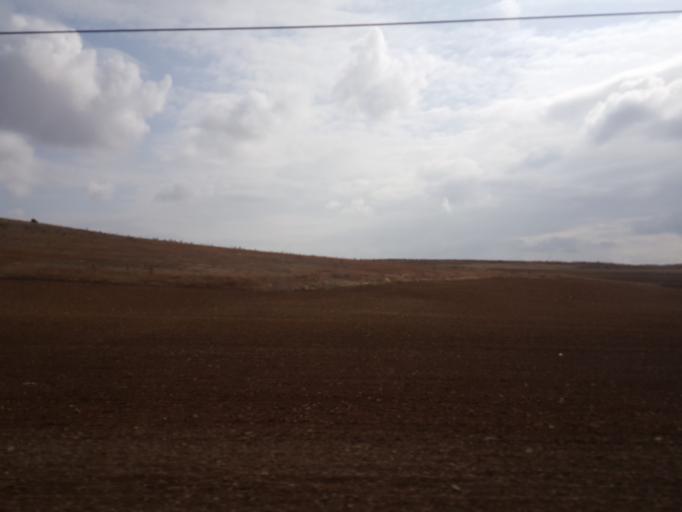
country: TR
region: Kirikkale
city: Keskin
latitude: 39.5854
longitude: 33.5993
